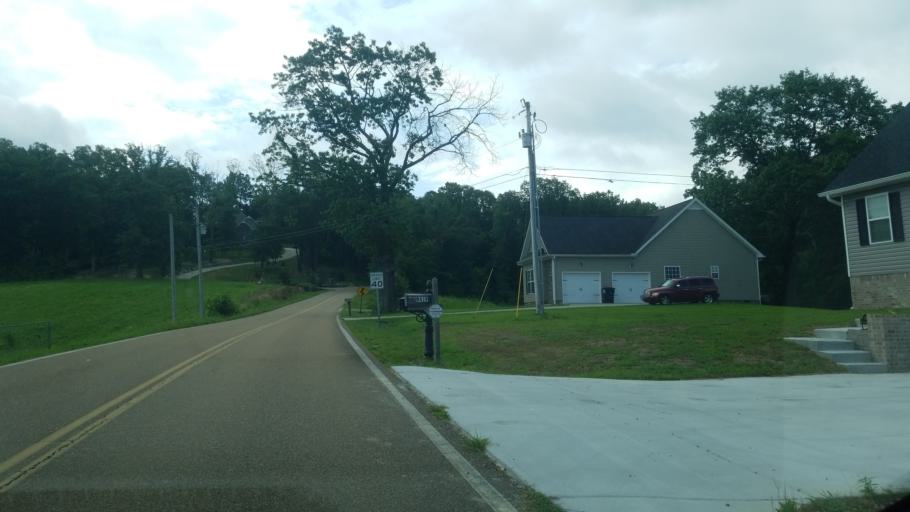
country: US
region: Tennessee
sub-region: Hamilton County
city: Lakesite
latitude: 35.2082
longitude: -85.0789
